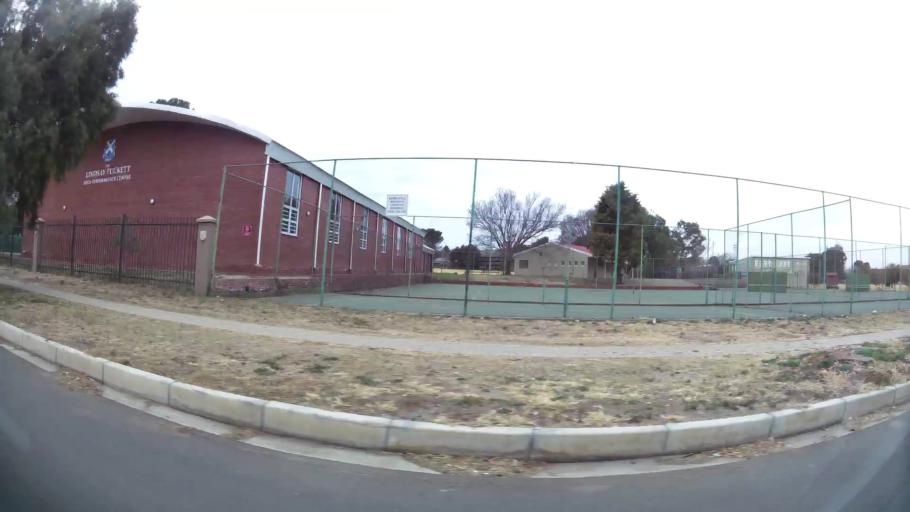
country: ZA
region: Orange Free State
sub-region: Mangaung Metropolitan Municipality
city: Bloemfontein
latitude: -29.1039
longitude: 26.2039
